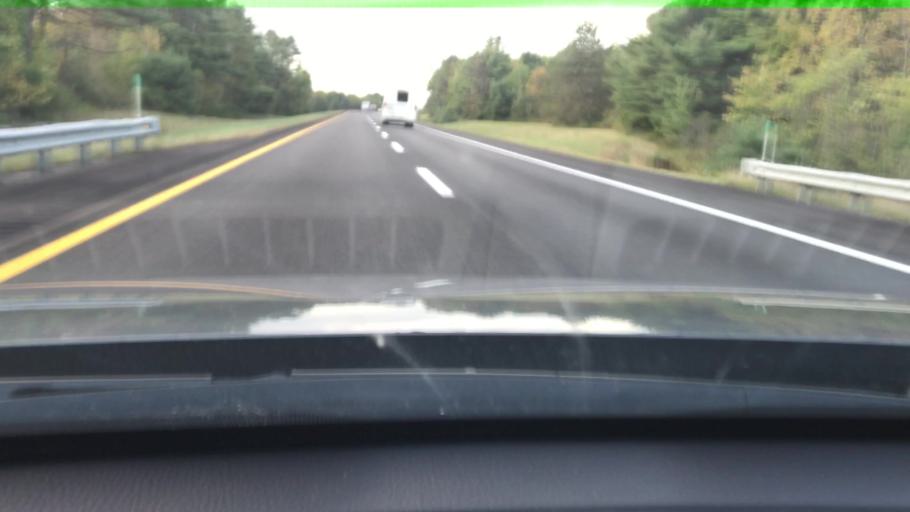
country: US
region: Maine
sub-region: Sagadahoc County
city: Richmond
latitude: 44.0701
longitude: -69.8814
